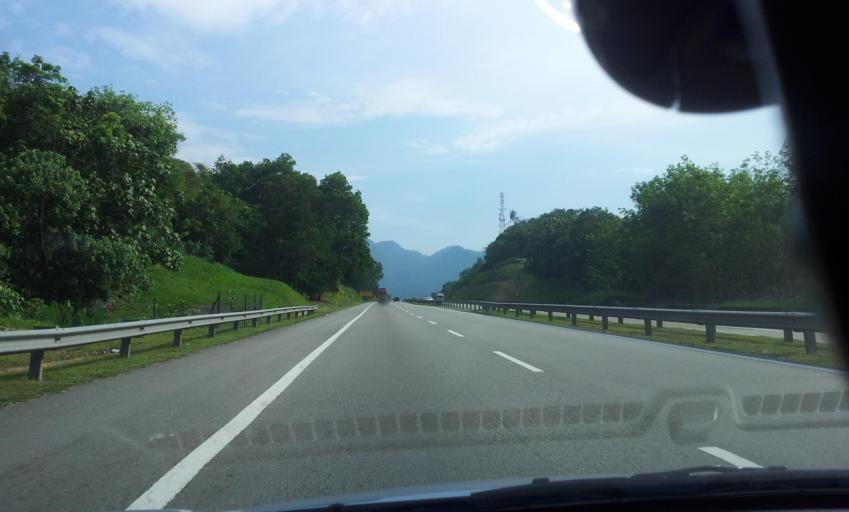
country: MY
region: Pahang
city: Bentong Town
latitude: 3.4555
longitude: 102.0378
